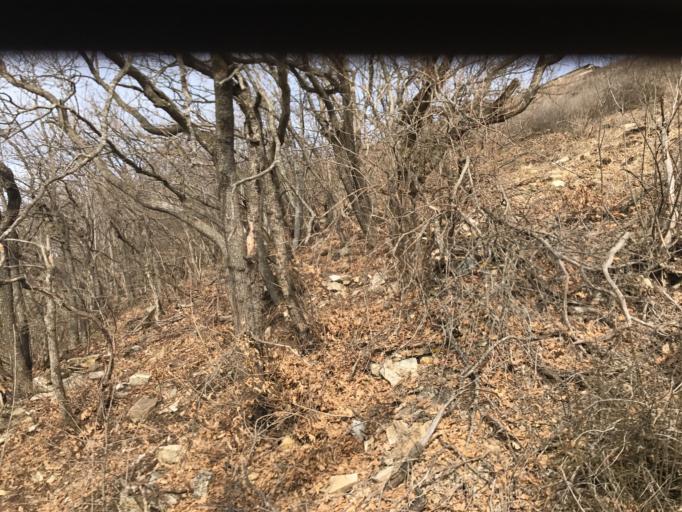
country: RU
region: Stavropol'skiy
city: Goryachevodskiy
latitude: 44.0492
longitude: 43.0882
